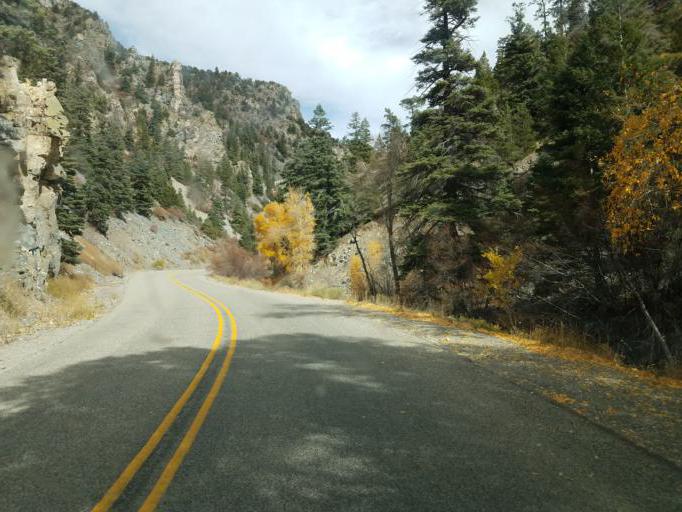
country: US
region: New Mexico
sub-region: Taos County
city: Arroyo Seco
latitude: 36.5461
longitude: -105.5524
